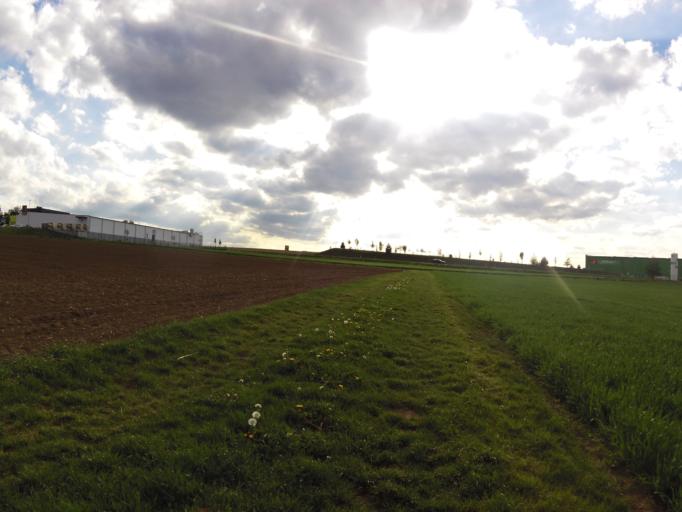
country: DE
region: Bavaria
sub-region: Regierungsbezirk Unterfranken
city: Kurnach
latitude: 49.8483
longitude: 10.0303
